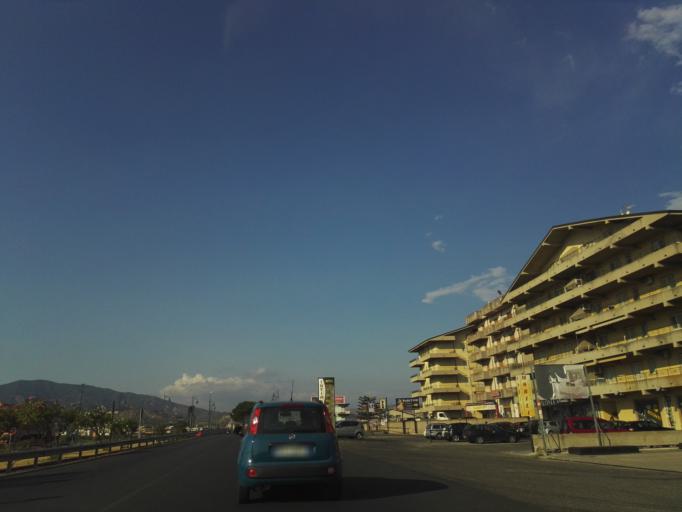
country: IT
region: Calabria
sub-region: Provincia di Reggio Calabria
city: Marina di Gioiosa Ionica
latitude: 38.2930
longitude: 16.3205
